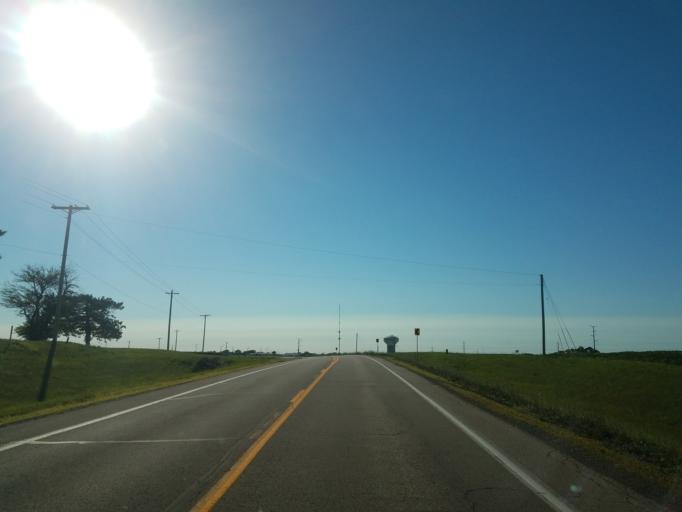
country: US
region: Illinois
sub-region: McLean County
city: Bloomington
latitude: 40.4469
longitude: -88.9531
